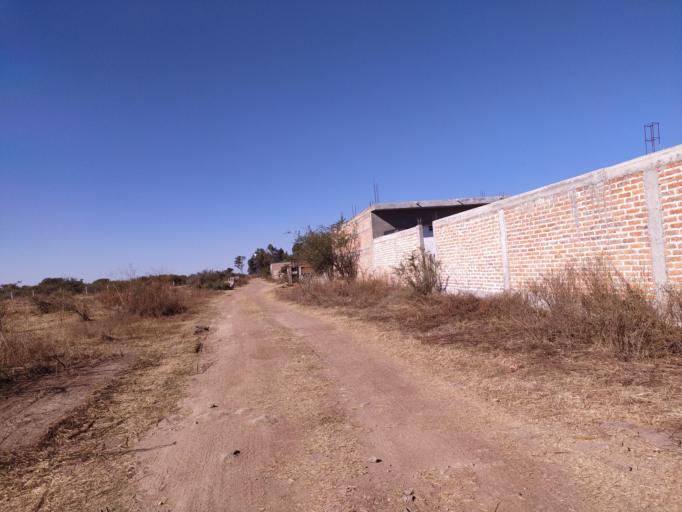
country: MX
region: Guanajuato
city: Ciudad Manuel Doblado
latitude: 20.8084
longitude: -101.9980
